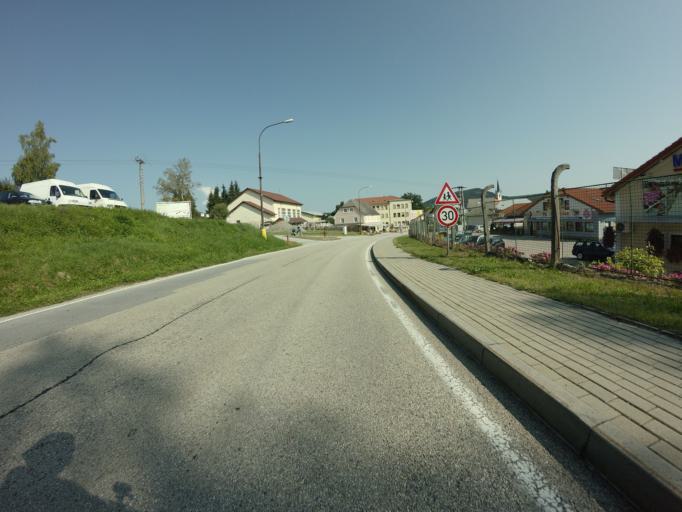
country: CZ
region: Jihocesky
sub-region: Okres Cesky Krumlov
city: Vyssi Brod
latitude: 48.6118
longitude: 14.3114
